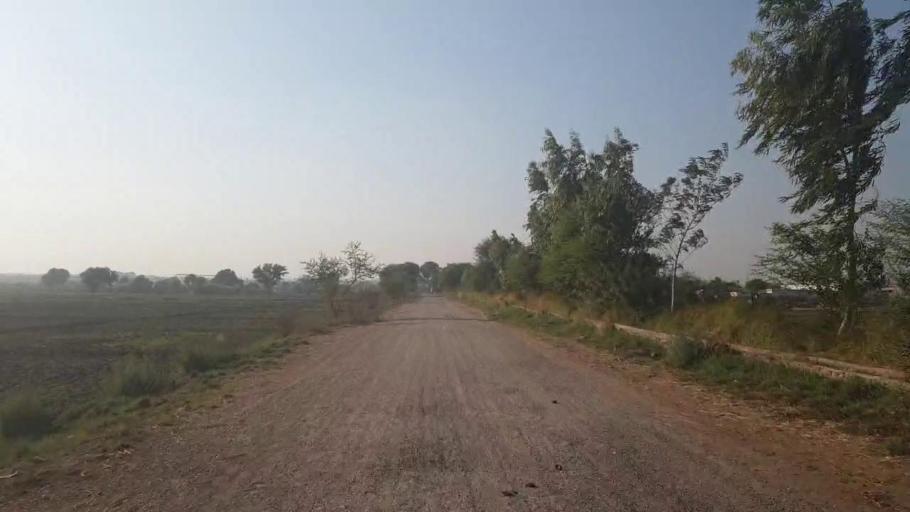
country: PK
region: Sindh
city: Jamshoro
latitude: 25.4006
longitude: 68.2929
